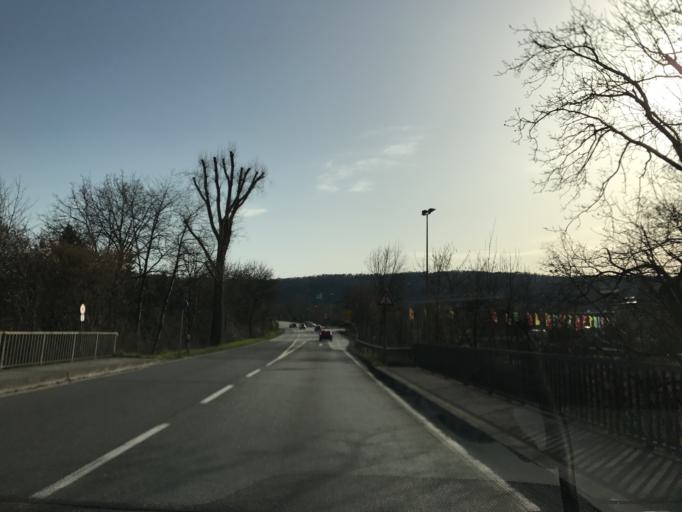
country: DE
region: Rheinland-Pfalz
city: Unkel
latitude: 50.5956
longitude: 7.2230
